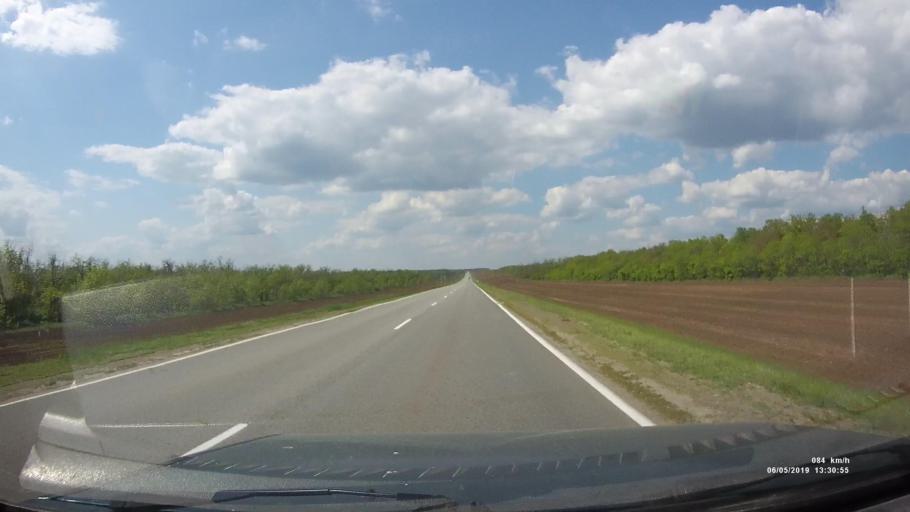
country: RU
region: Rostov
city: Ust'-Donetskiy
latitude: 47.6729
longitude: 40.8184
